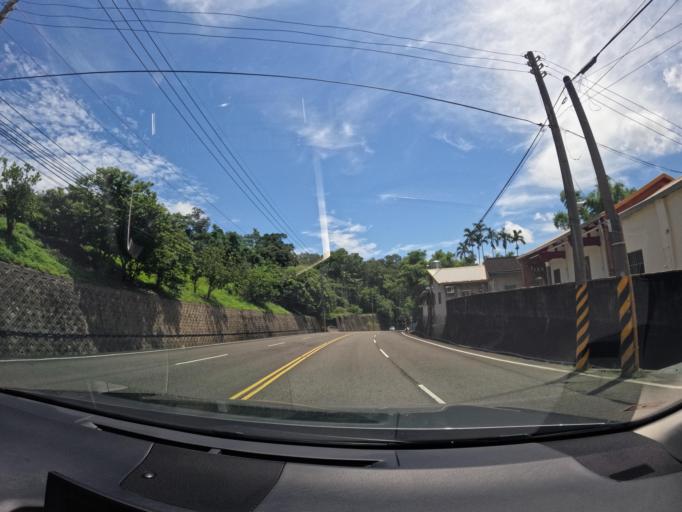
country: TW
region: Taiwan
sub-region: Miaoli
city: Miaoli
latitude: 24.5657
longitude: 120.9332
